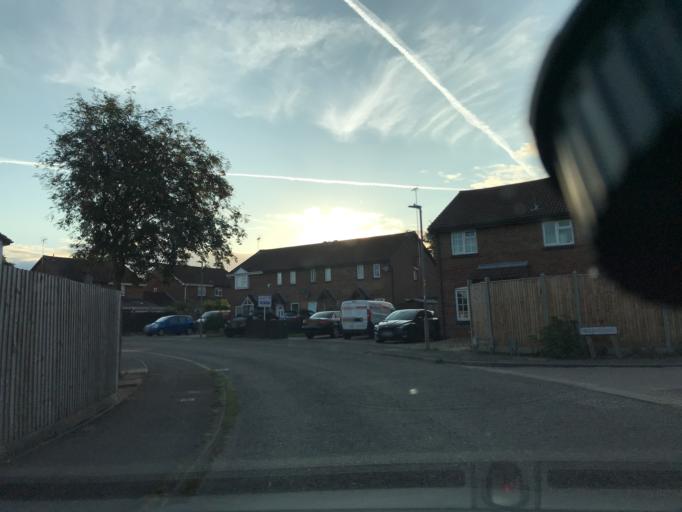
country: GB
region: England
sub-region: Buckinghamshire
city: Aylesbury
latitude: 51.8239
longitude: -0.7916
